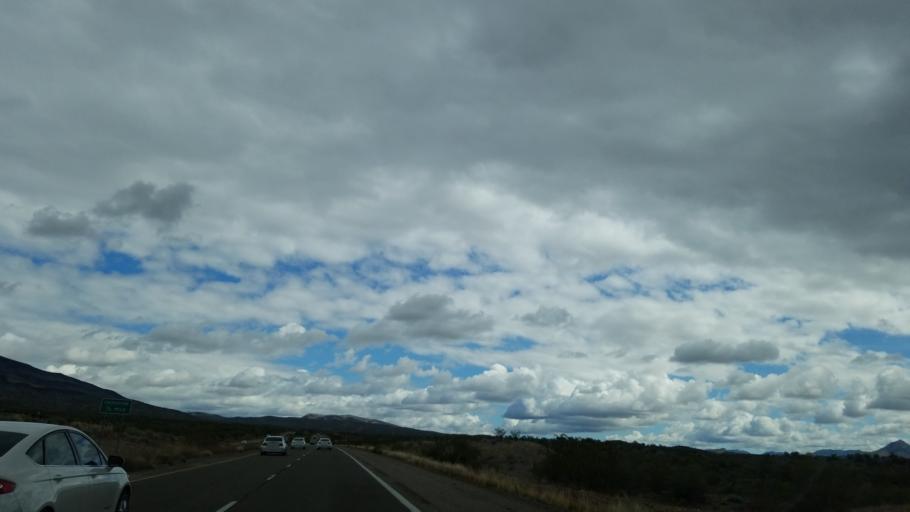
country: US
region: Arizona
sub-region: Yavapai County
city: Bagdad
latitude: 34.6347
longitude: -113.5514
